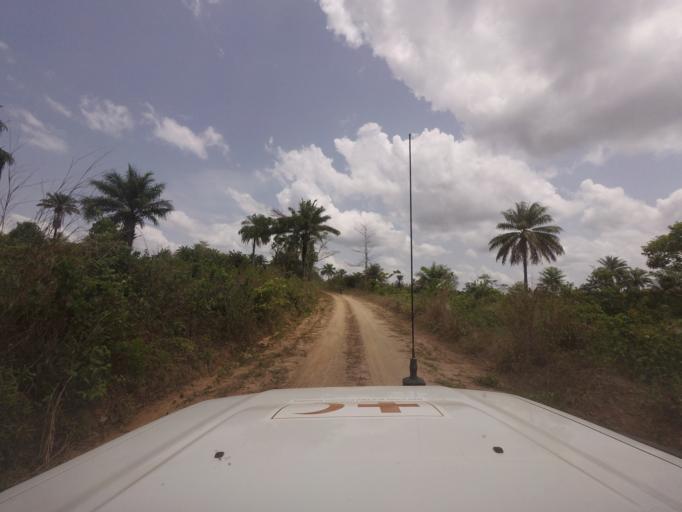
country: GN
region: Nzerekore
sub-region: Yomou
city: Yomou
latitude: 7.2637
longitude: -9.1878
